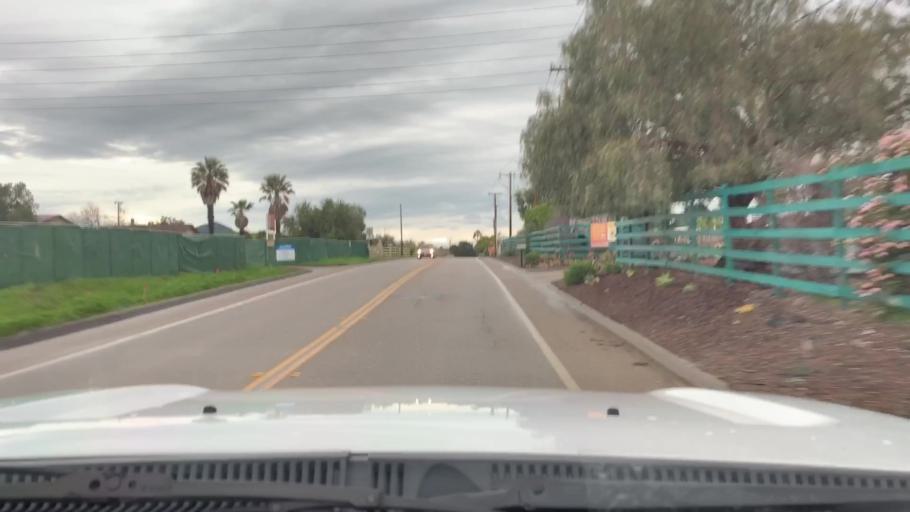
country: US
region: California
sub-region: San Luis Obispo County
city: San Luis Obispo
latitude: 35.2603
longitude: -120.6346
